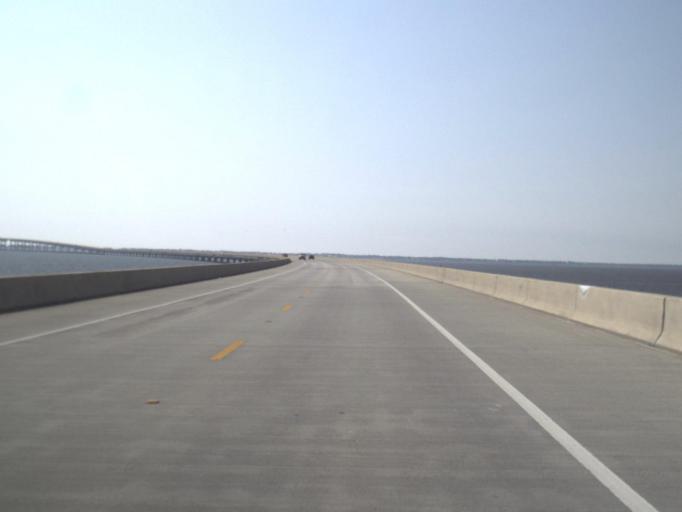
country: US
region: Florida
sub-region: Franklin County
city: Eastpoint
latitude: 29.7018
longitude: -84.8904
